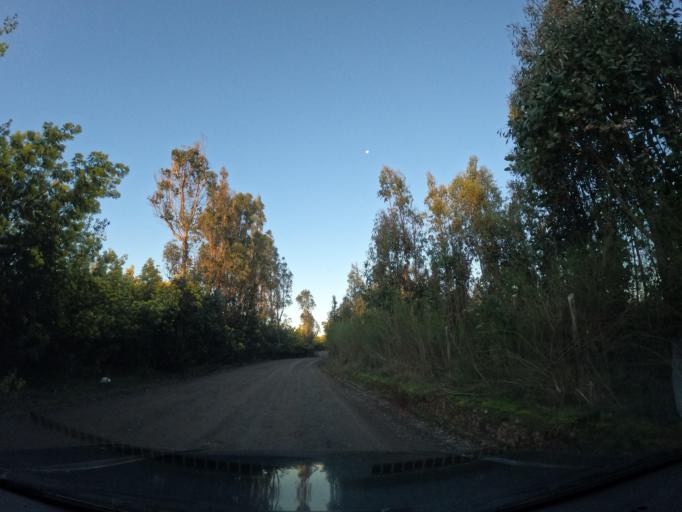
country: CL
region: Biobio
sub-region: Provincia de Concepcion
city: Chiguayante
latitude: -37.0117
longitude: -72.8802
